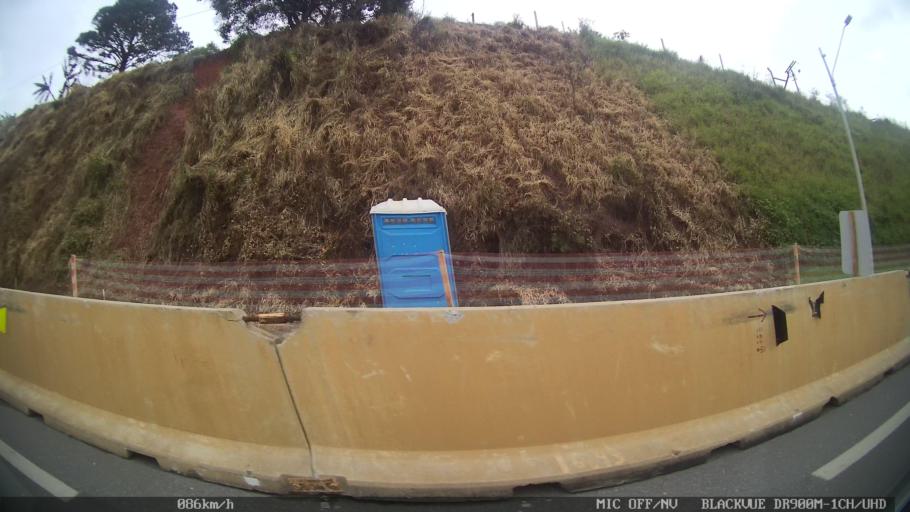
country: BR
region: Santa Catarina
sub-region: Biguacu
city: Biguacu
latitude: -27.5183
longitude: -48.6387
